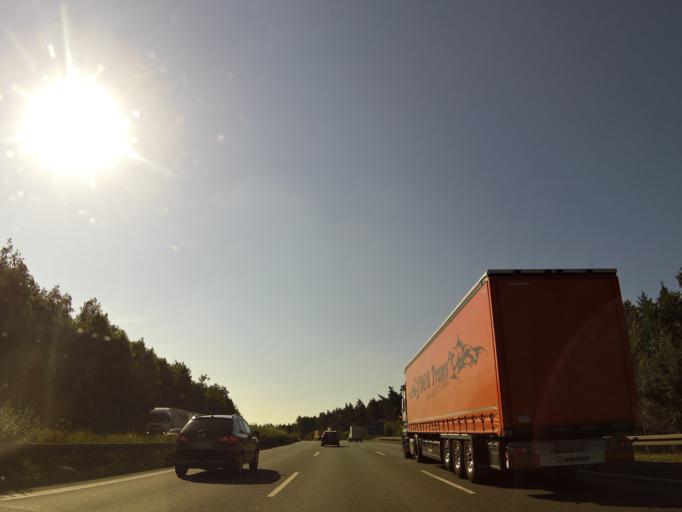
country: DE
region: Bavaria
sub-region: Regierungsbezirk Mittelfranken
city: Schwaig
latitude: 49.4677
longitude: 11.1892
